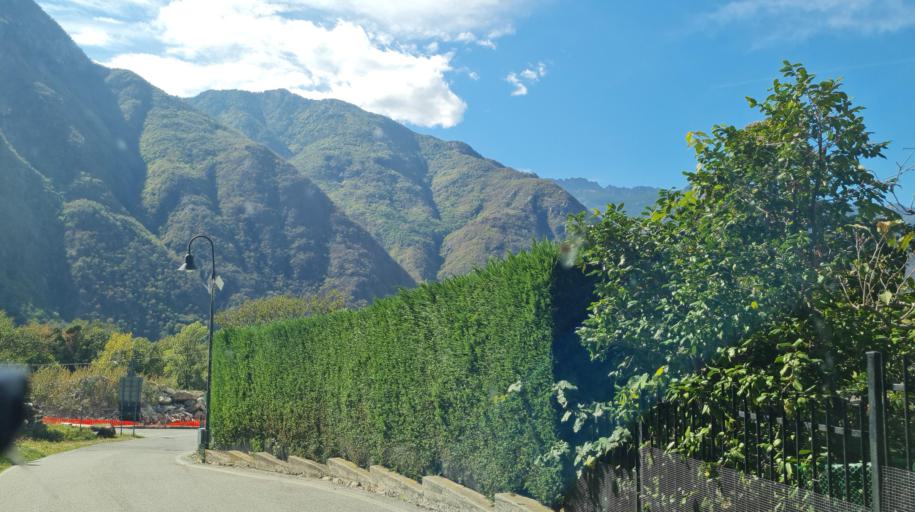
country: IT
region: Aosta Valley
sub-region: Valle d'Aosta
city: Arnad
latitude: 45.6395
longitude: 7.7286
